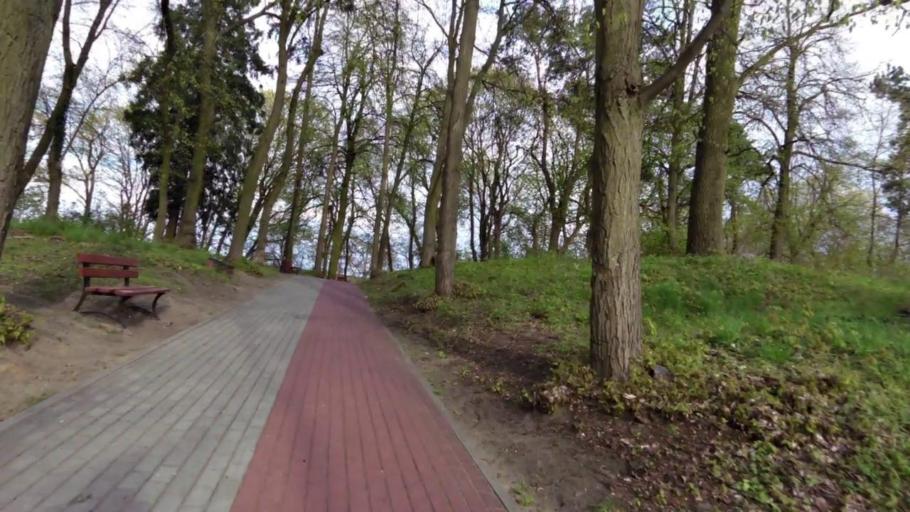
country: PL
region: West Pomeranian Voivodeship
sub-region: Powiat mysliborski
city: Barlinek
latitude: 52.9883
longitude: 15.2157
